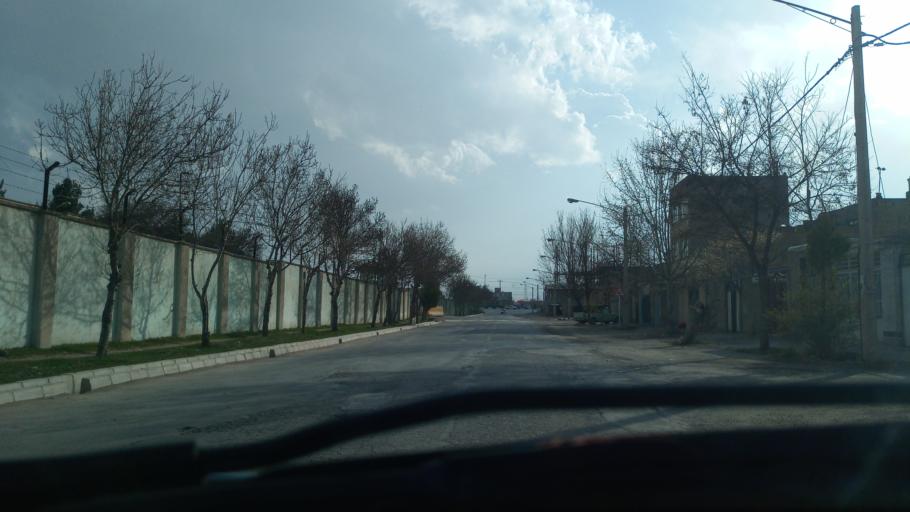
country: IR
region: Razavi Khorasan
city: Quchan
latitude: 37.1015
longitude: 58.4965
